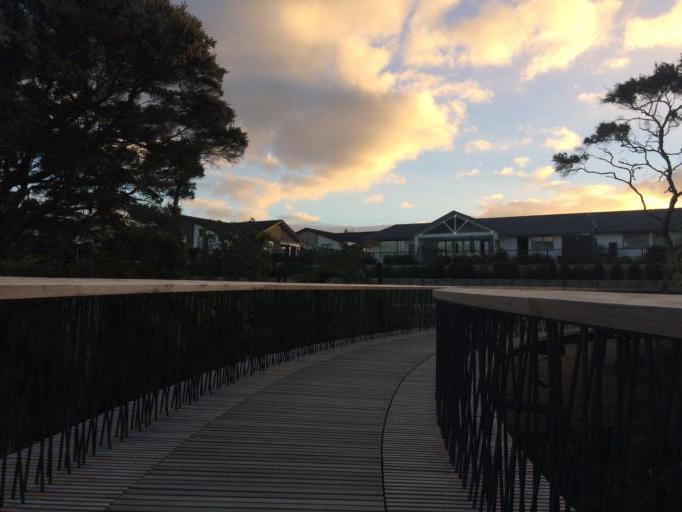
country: NZ
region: Auckland
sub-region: Auckland
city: Rosebank
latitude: -36.7890
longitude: 174.6608
